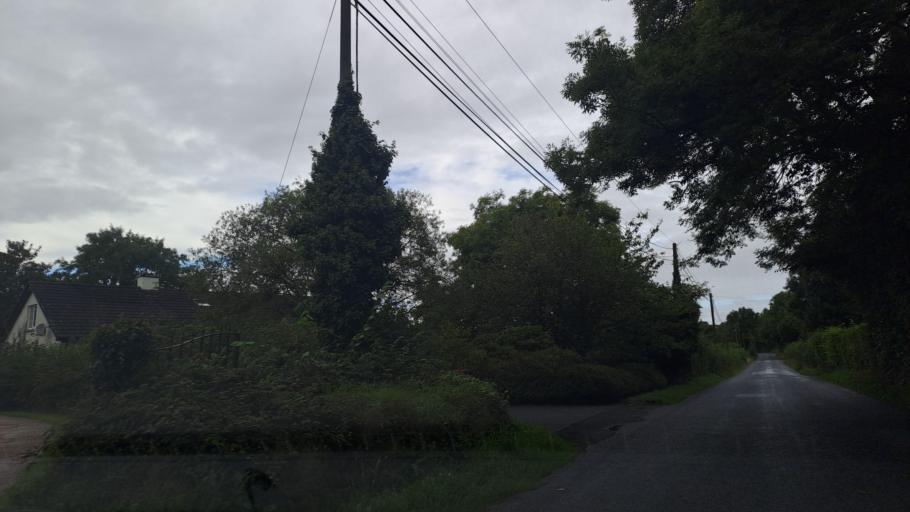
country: IE
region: Ulster
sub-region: County Monaghan
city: Carrickmacross
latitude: 53.9674
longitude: -6.7447
